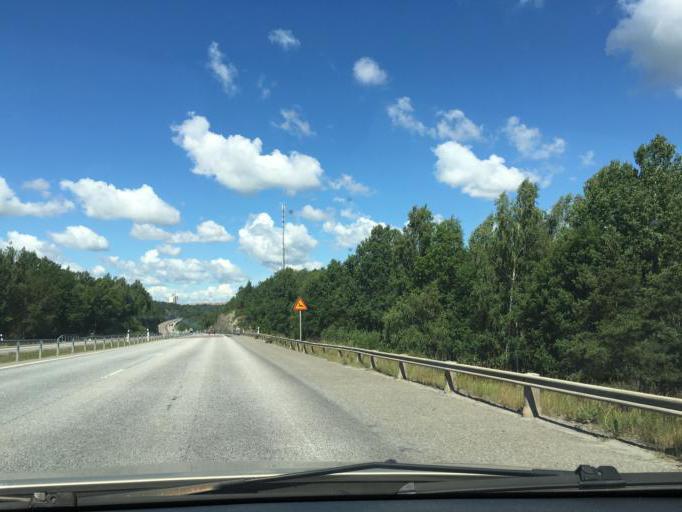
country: SE
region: Stockholm
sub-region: Nacka Kommun
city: Alta
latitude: 59.2965
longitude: 18.2021
